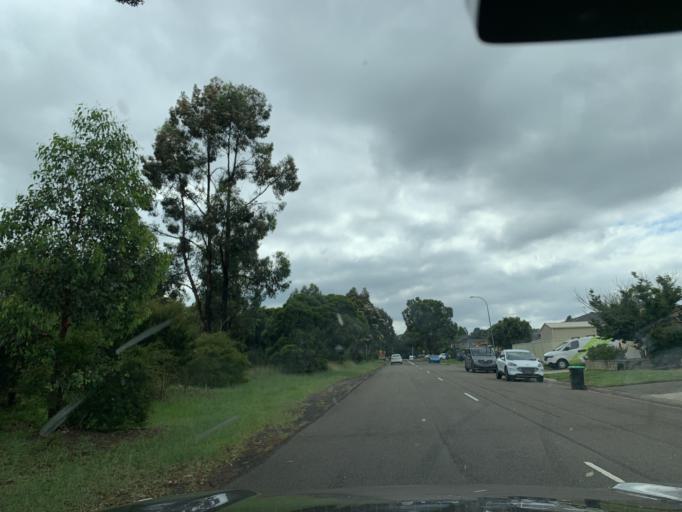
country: AU
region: New South Wales
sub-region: Penrith Municipality
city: Werrington Downs
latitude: -33.7052
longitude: 150.7198
